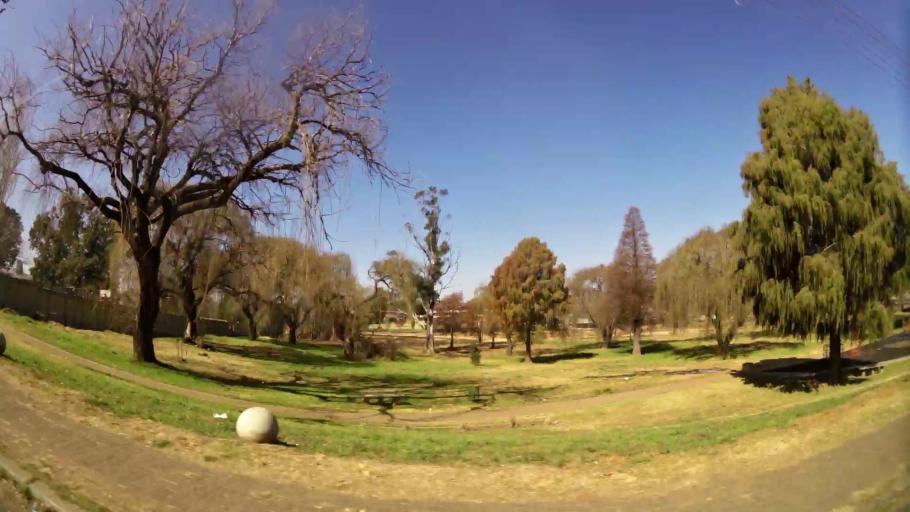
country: ZA
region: Gauteng
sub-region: City of Johannesburg Metropolitan Municipality
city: Johannesburg
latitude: -26.1898
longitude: 27.9588
